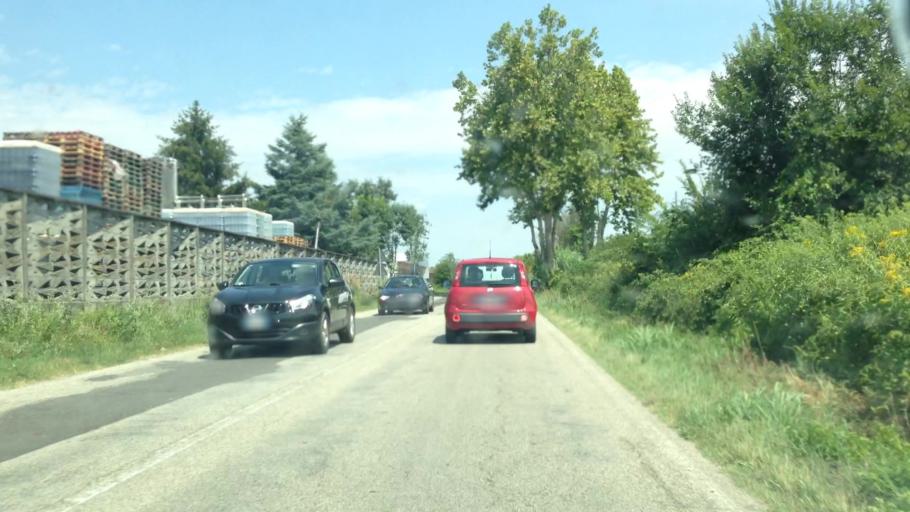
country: IT
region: Piedmont
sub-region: Provincia di Asti
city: Portacomaro
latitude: 44.9388
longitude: 8.2247
